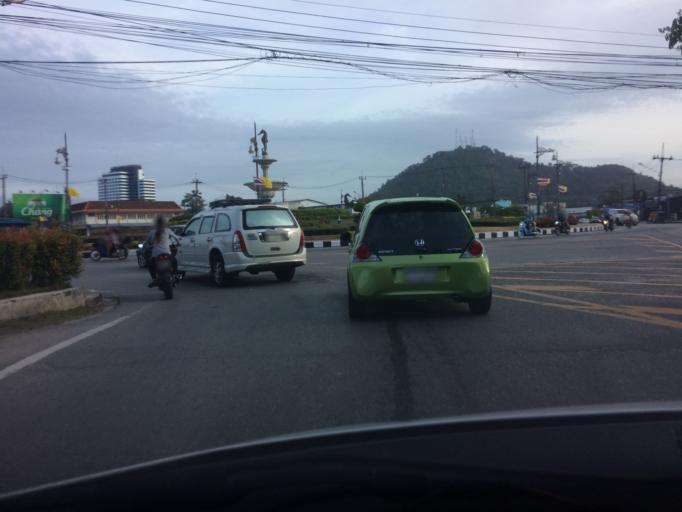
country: TH
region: Phuket
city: Ban Talat Yai
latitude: 7.8784
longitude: 98.3986
